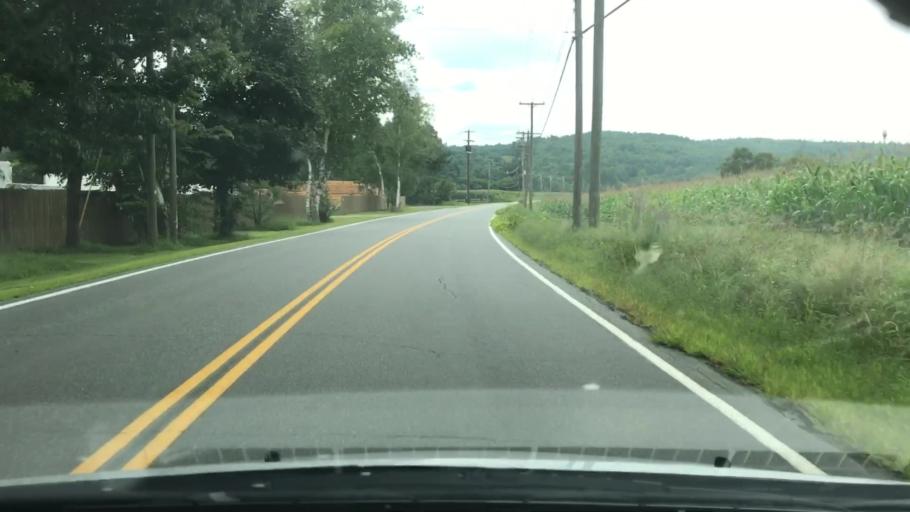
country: US
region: New Hampshire
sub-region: Grafton County
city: Woodsville
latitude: 44.1408
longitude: -72.0347
